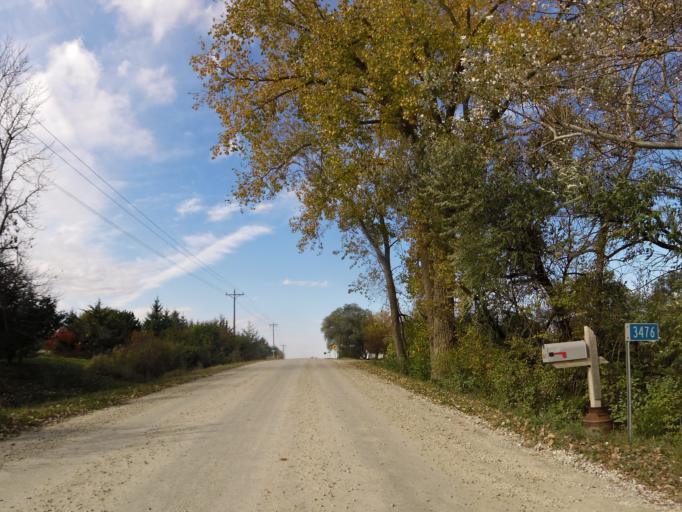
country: US
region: Minnesota
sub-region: Scott County
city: Prior Lake
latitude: 44.6887
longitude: -93.4510
